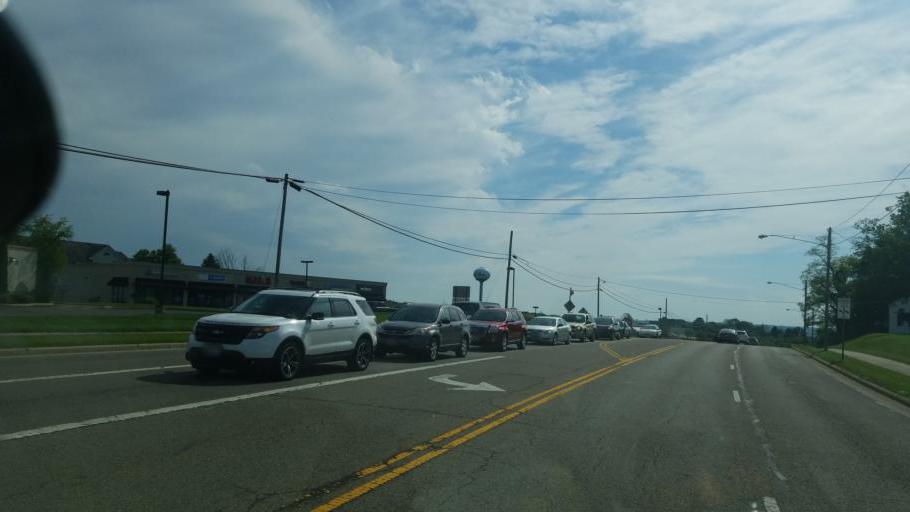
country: US
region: Ohio
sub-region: Knox County
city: Gambier
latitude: 40.4029
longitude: -82.4376
